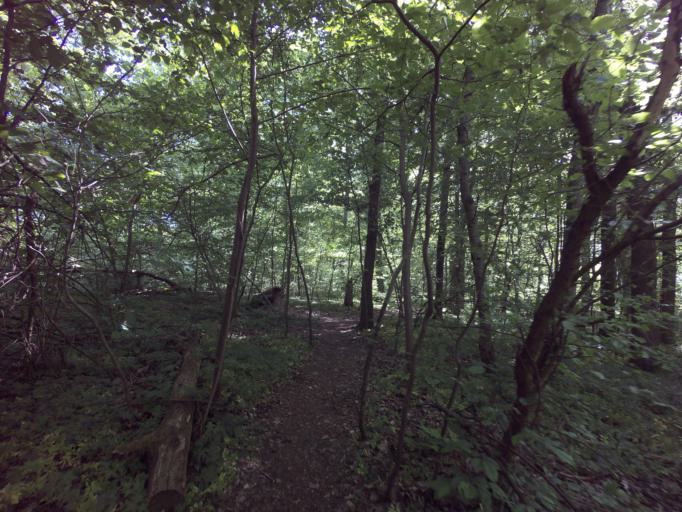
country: DE
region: Lower Saxony
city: Lehre
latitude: 52.2970
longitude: 10.6663
